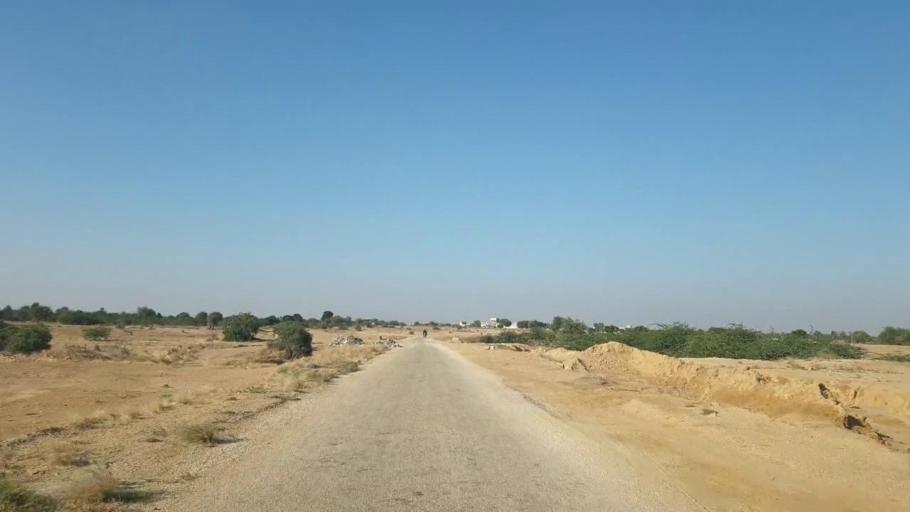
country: PK
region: Sindh
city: Malir Cantonment
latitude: 25.4295
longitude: 67.4608
